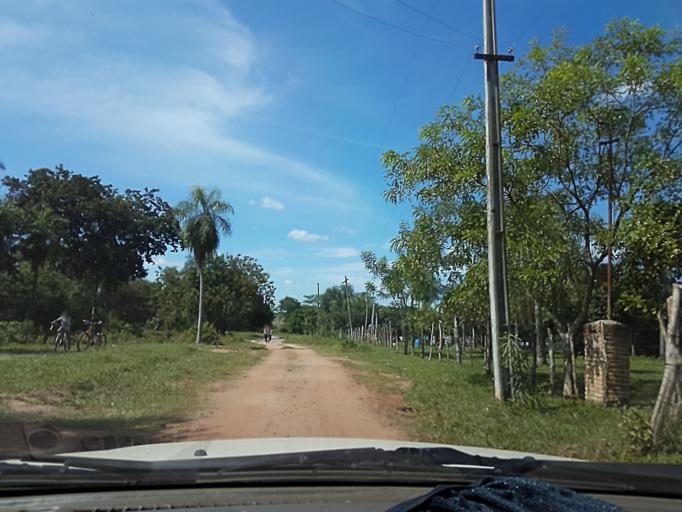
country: PY
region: Cordillera
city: Arroyos y Esteros
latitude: -24.9804
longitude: -57.1976
